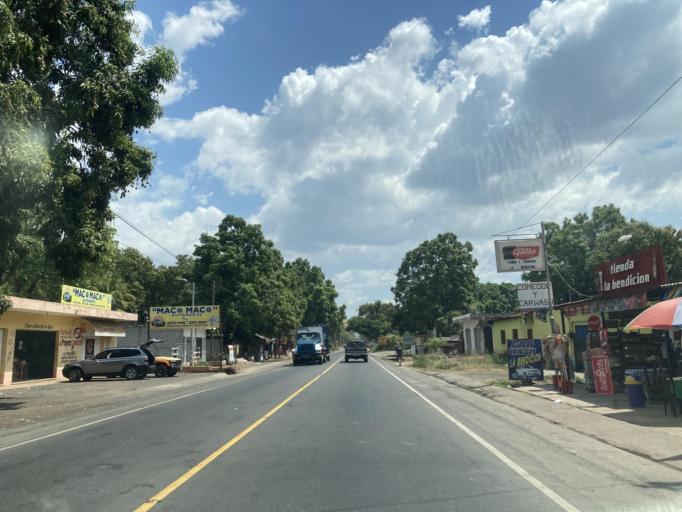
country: GT
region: Santa Rosa
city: Guazacapan
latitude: 14.0672
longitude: -90.4007
